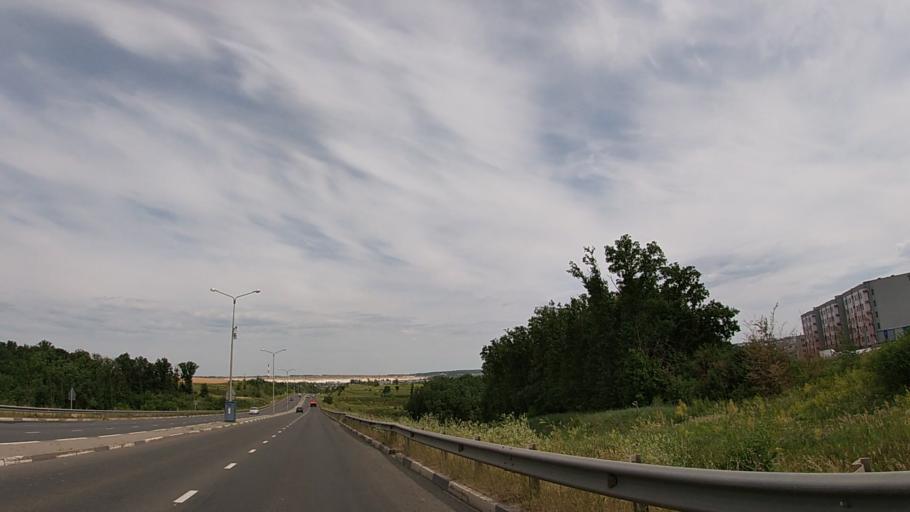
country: RU
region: Belgorod
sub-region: Belgorodskiy Rayon
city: Belgorod
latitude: 50.5986
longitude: 36.5303
